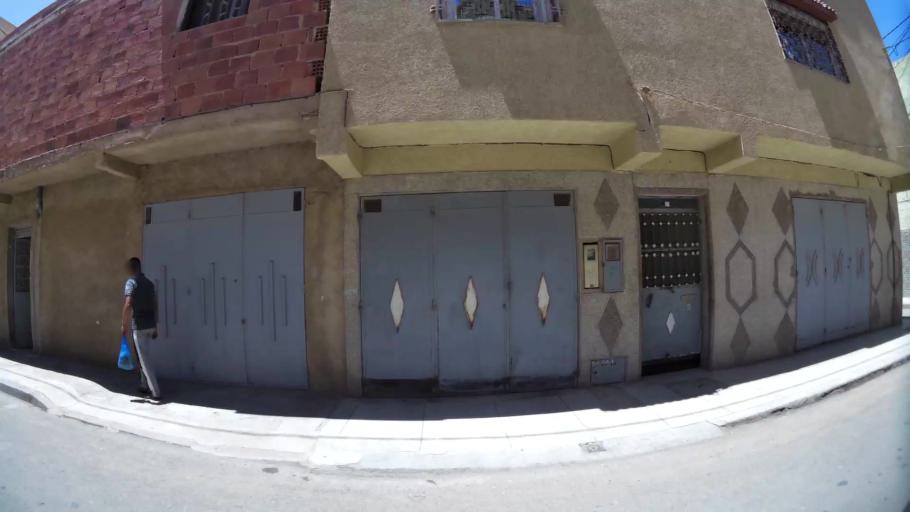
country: MA
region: Oriental
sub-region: Oujda-Angad
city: Oujda
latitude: 34.6611
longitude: -1.9261
